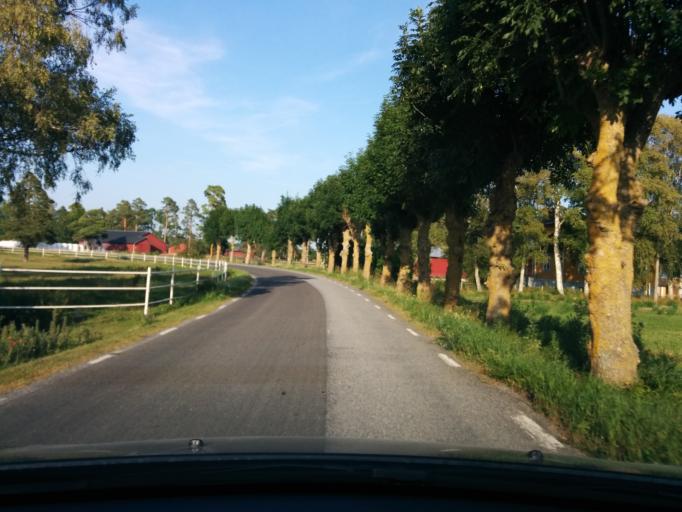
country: SE
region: Gotland
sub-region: Gotland
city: Visby
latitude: 57.5142
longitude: 18.5649
